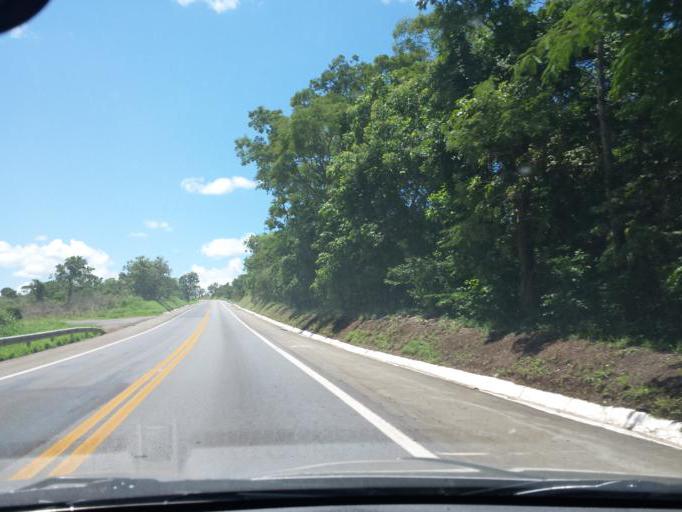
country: BR
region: Goias
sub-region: Luziania
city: Luziania
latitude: -16.4222
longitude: -47.8247
